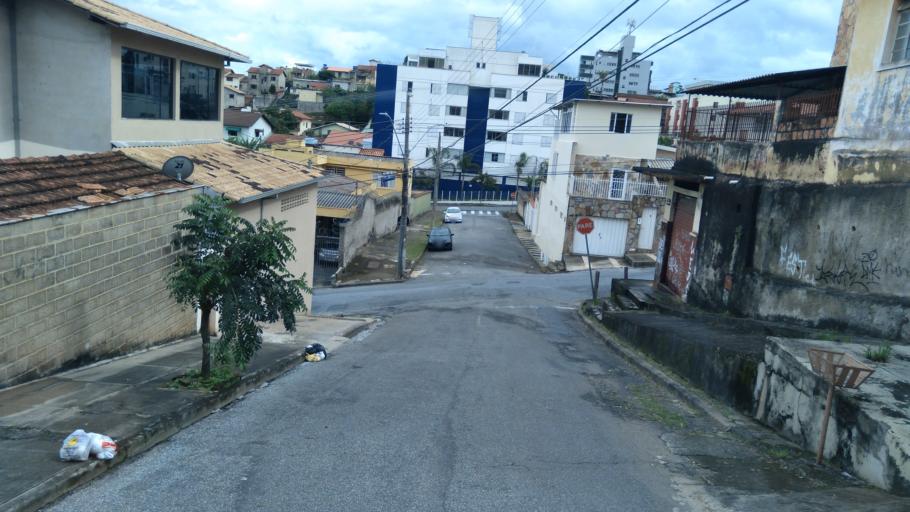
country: BR
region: Minas Gerais
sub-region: Belo Horizonte
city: Belo Horizonte
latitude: -19.9251
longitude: -43.9054
